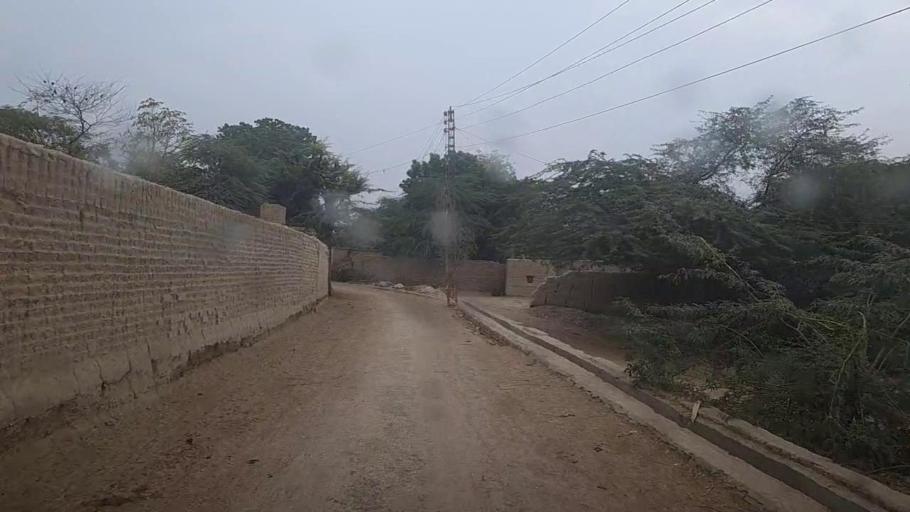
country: PK
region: Sindh
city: Gambat
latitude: 27.3591
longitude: 68.5975
